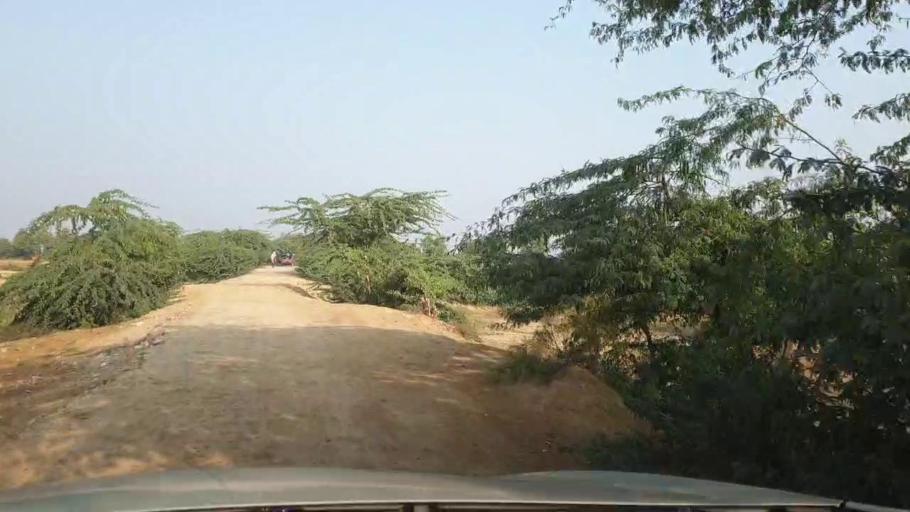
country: PK
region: Sindh
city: Sehwan
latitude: 26.3452
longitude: 67.7240
